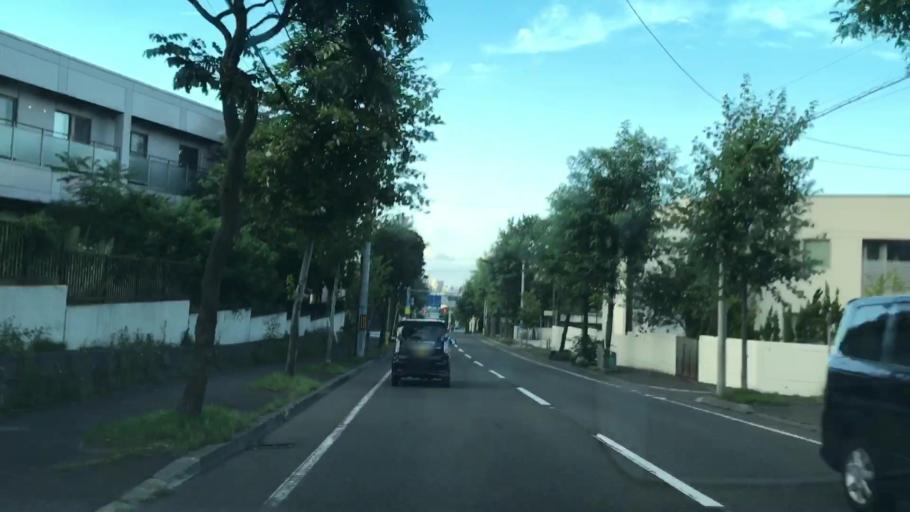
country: JP
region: Hokkaido
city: Sapporo
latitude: 43.0567
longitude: 141.2998
